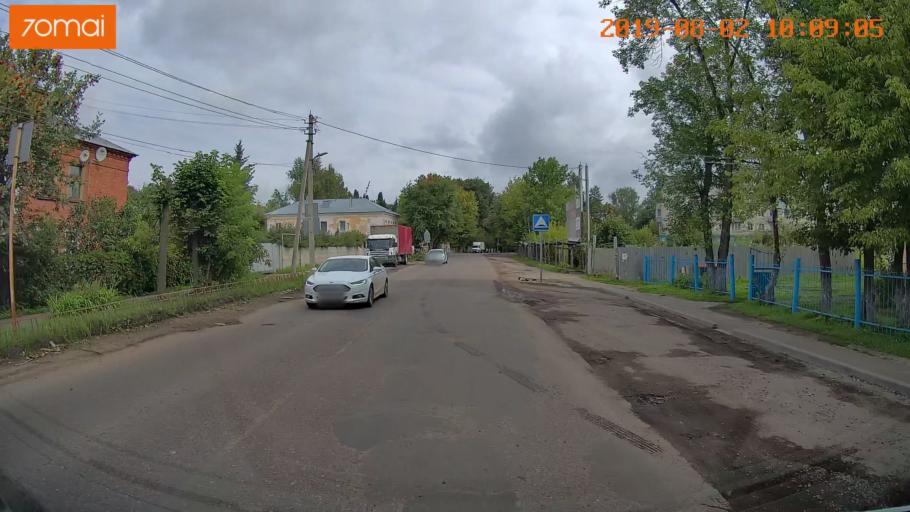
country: RU
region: Ivanovo
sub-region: Gorod Ivanovo
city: Ivanovo
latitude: 56.9863
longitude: 40.9446
